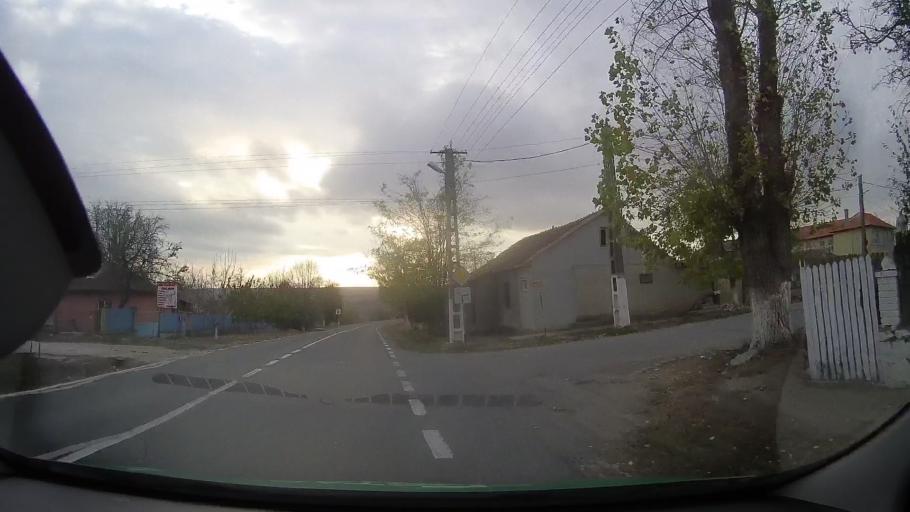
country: RO
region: Constanta
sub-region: Comuna Adamclisi
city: Adamclisi
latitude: 44.0831
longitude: 27.9550
